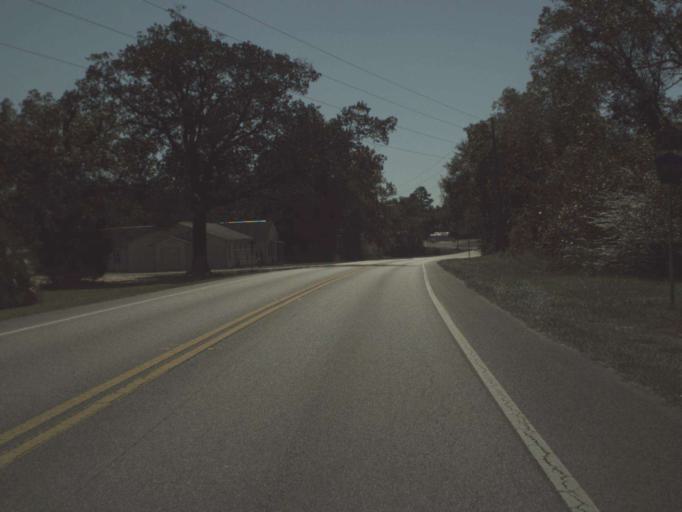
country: US
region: Florida
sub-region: Walton County
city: DeFuniak Springs
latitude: 30.8646
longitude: -86.1161
